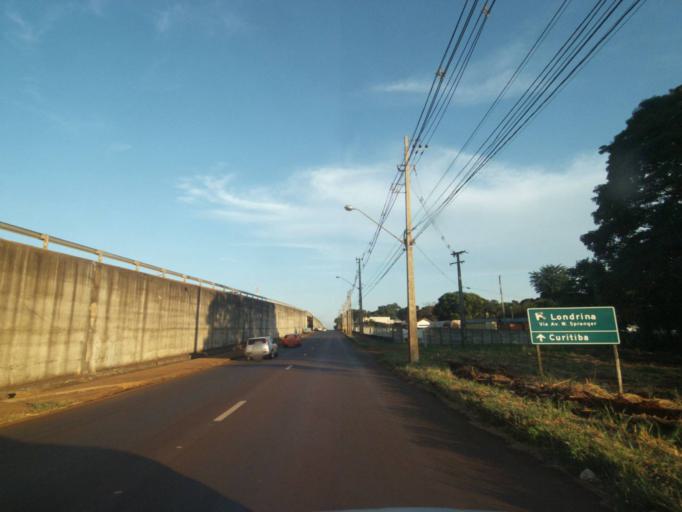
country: BR
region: Parana
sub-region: Londrina
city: Londrina
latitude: -23.3467
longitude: -51.1739
